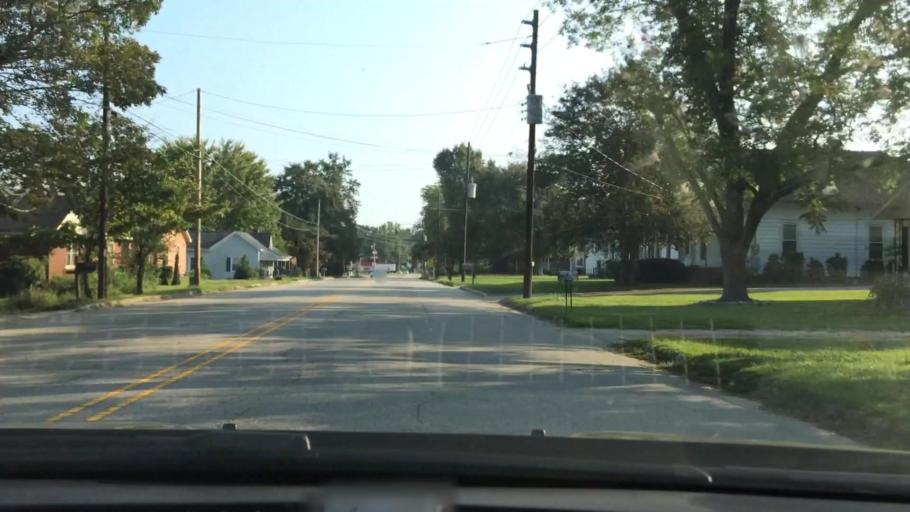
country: US
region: North Carolina
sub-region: Nash County
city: Spring Hope
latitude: 35.7833
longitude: -78.1182
